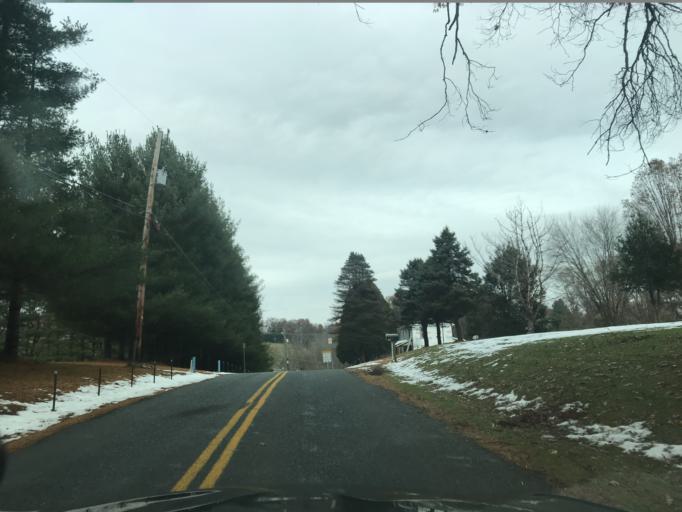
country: US
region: Pennsylvania
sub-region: York County
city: Susquehanna Trails
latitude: 39.6889
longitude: -76.4197
